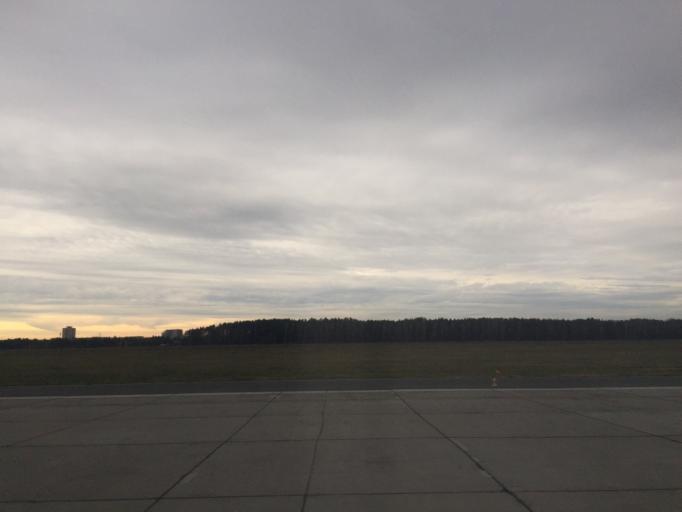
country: PL
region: Kujawsko-Pomorskie
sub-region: Bydgoszcz
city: Bydgoszcz
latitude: 53.0983
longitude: 17.9945
